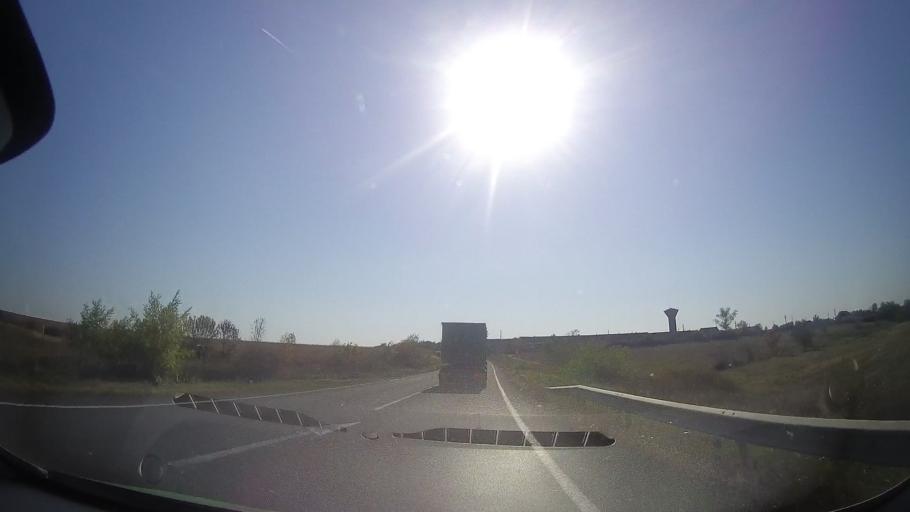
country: RO
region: Timis
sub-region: Comuna Belint
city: Belint
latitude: 45.7732
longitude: 21.7026
